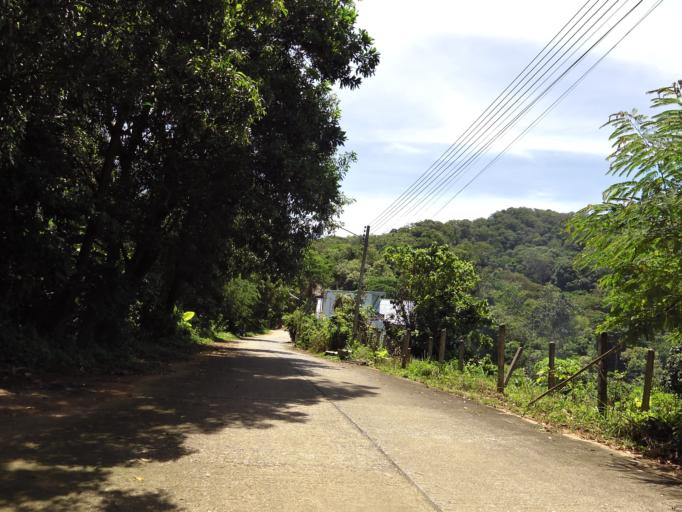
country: TH
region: Phuket
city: Ban Karon
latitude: 7.8473
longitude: 98.3039
